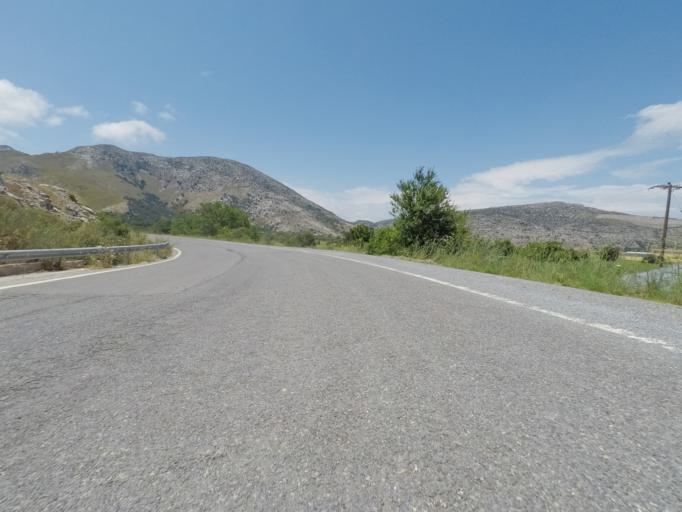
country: GR
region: Crete
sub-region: Nomos Irakleiou
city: Mokhos
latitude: 35.1780
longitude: 25.4411
